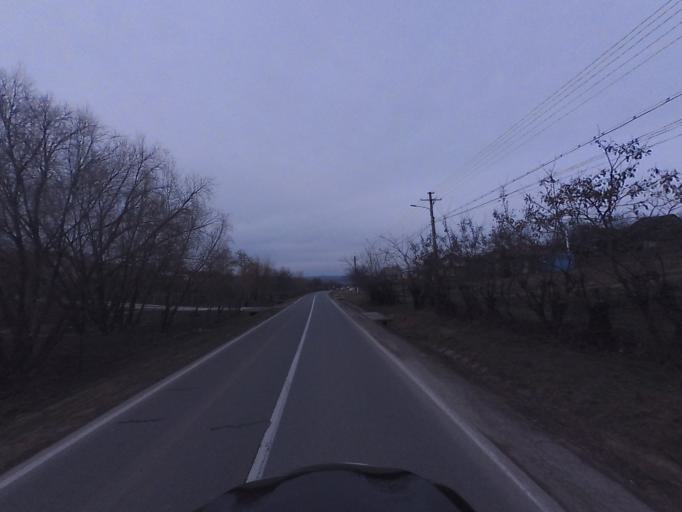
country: RO
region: Iasi
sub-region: Comuna Popricani
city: Popricani
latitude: 47.2893
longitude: 27.5122
